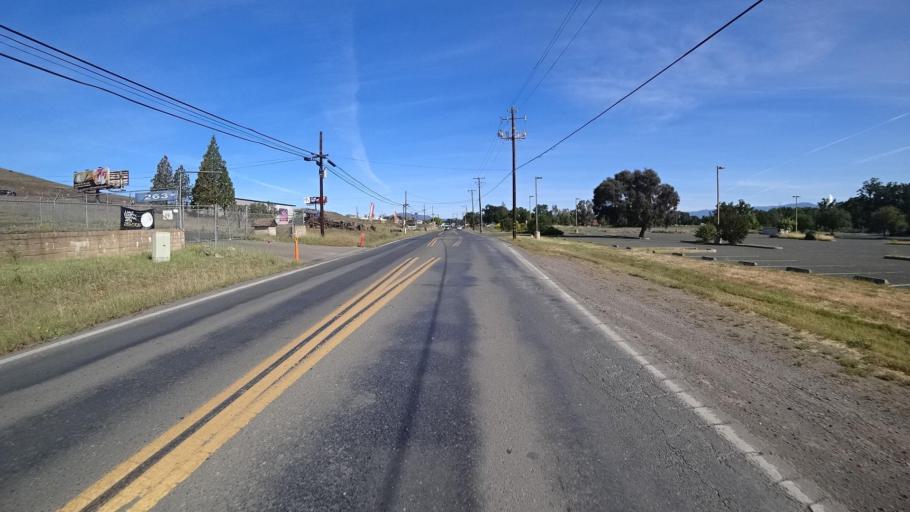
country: US
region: California
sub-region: Lake County
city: Lakeport
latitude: 39.0146
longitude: -122.9101
